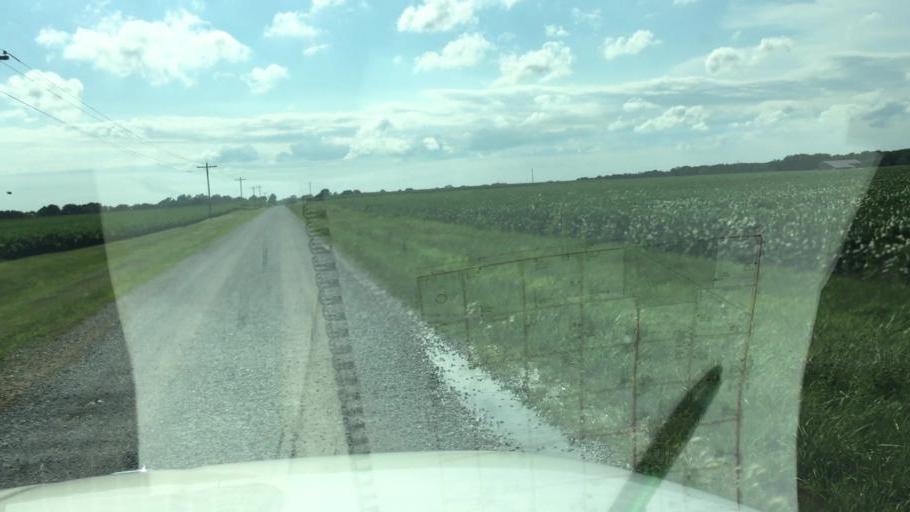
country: US
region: Illinois
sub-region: Hancock County
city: Nauvoo
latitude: 40.5215
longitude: -91.2938
